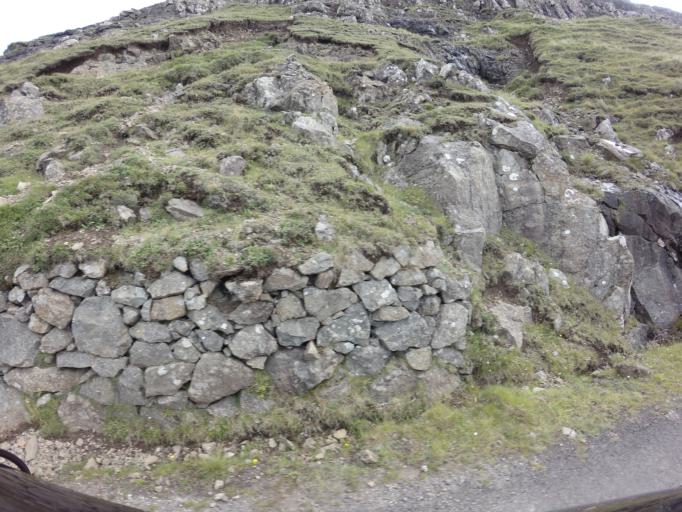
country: FO
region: Sandoy
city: Sandur
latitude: 61.8040
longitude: -6.7524
